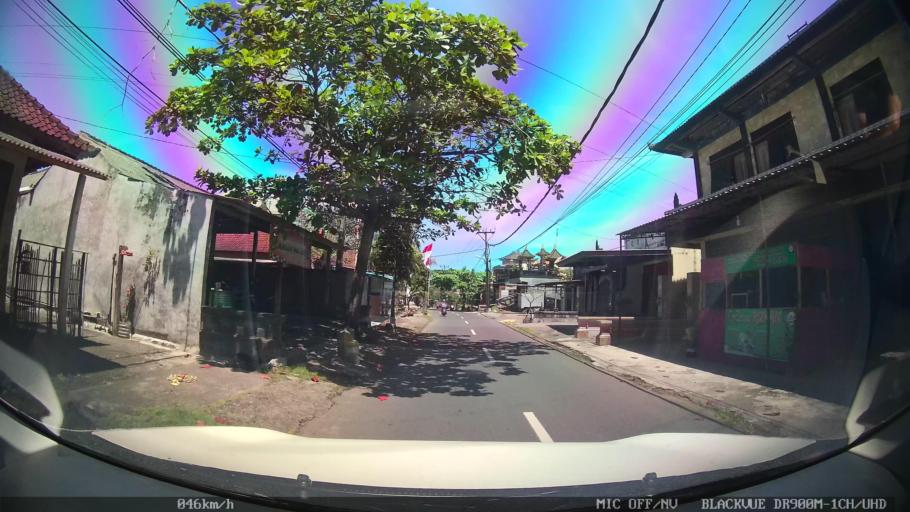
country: ID
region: Bali
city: Banjar Pasekan
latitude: -8.5707
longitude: 115.3219
